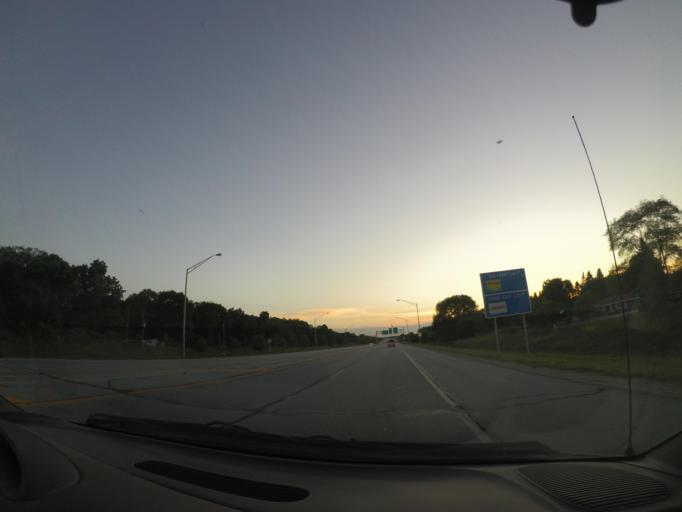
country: US
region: Indiana
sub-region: Elkhart County
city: Dunlap
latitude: 41.6672
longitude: -85.8706
